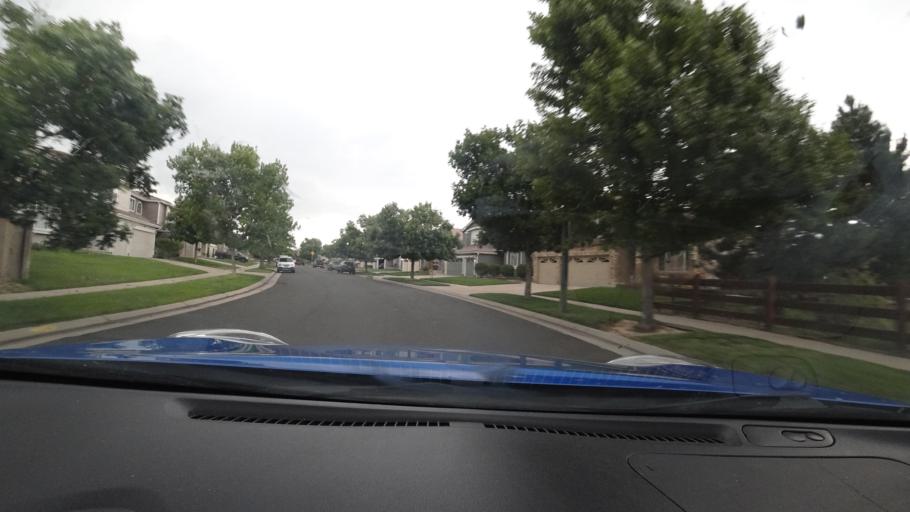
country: US
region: Colorado
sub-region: Adams County
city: Aurora
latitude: 39.7774
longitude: -104.7518
